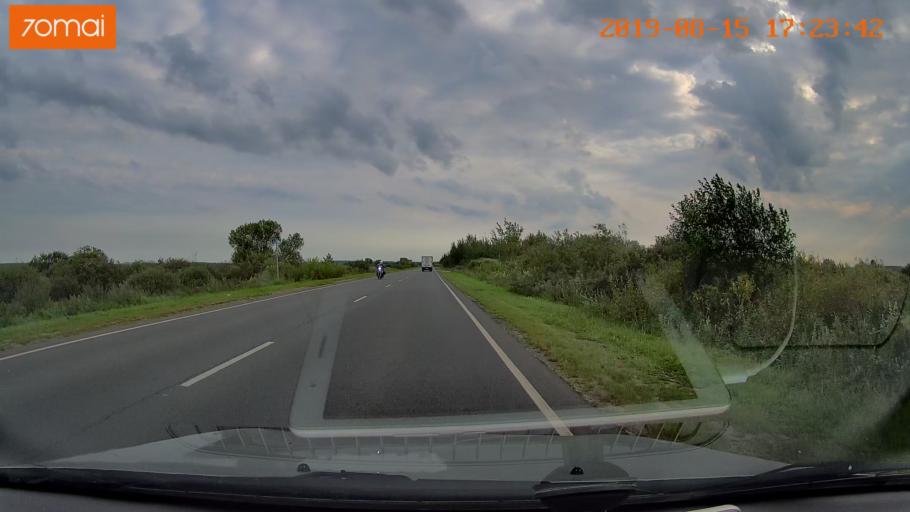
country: RU
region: Moskovskaya
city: Ashitkovo
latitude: 55.3977
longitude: 38.5548
